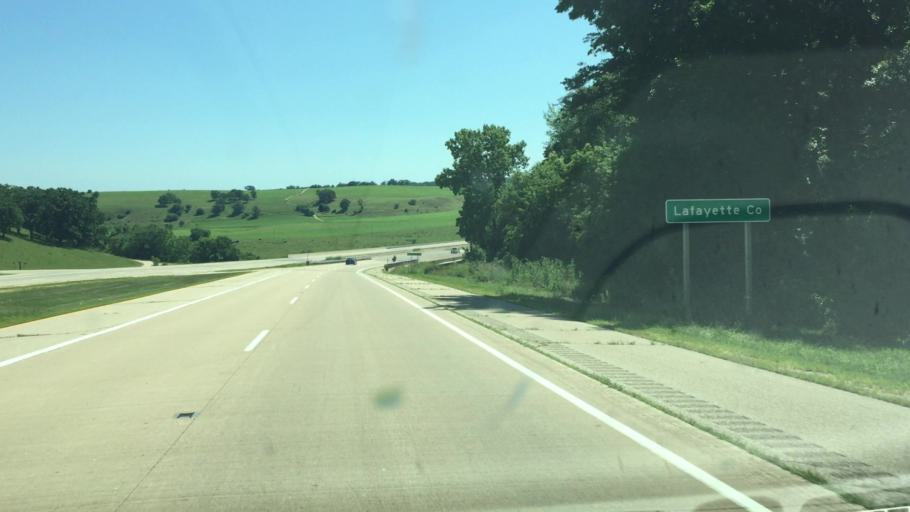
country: US
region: Wisconsin
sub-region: Iowa County
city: Mineral Point
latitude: 42.8146
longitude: -90.2575
